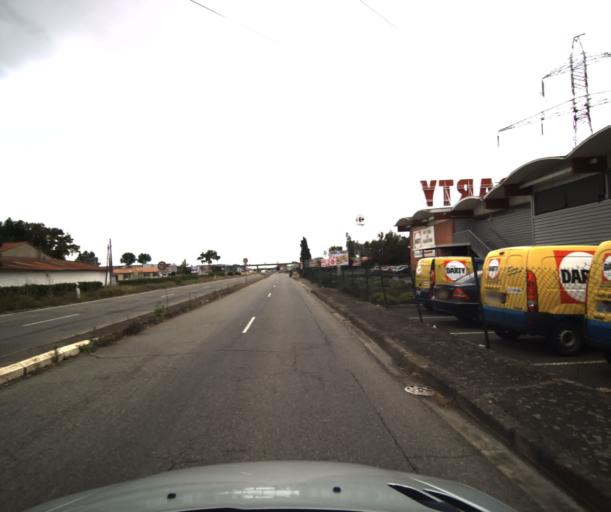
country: FR
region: Midi-Pyrenees
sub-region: Departement de la Haute-Garonne
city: Portet-sur-Garonne
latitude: 43.5317
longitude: 1.4065
